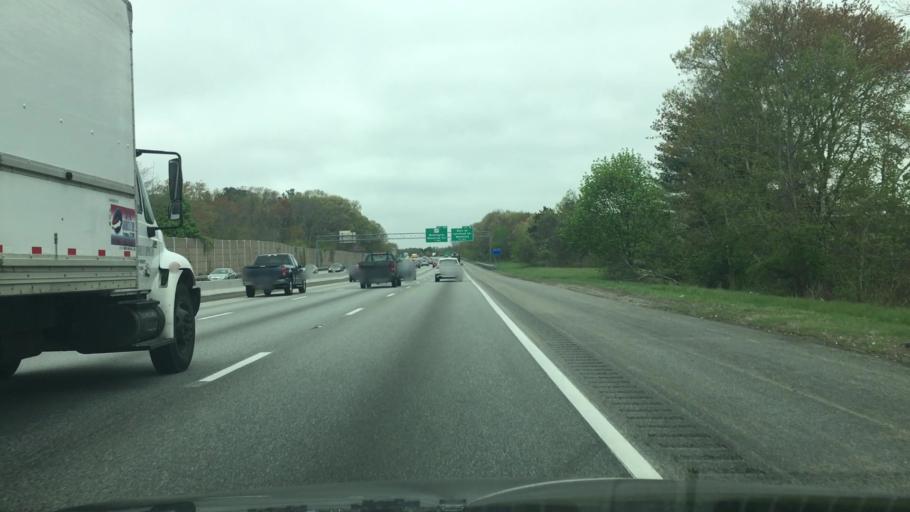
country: US
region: Massachusetts
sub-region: Essex County
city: Lynnfield
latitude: 42.5188
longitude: -71.0520
